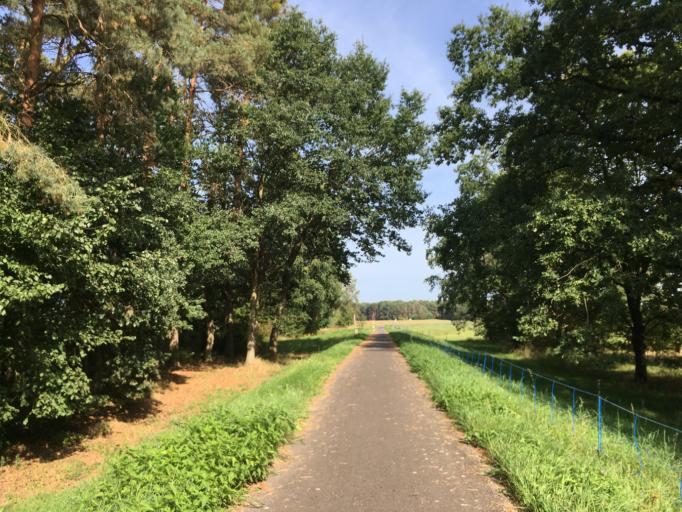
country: PL
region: Lubusz
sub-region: Powiat krosnienski
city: Gubin
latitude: 52.0181
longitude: 14.7310
